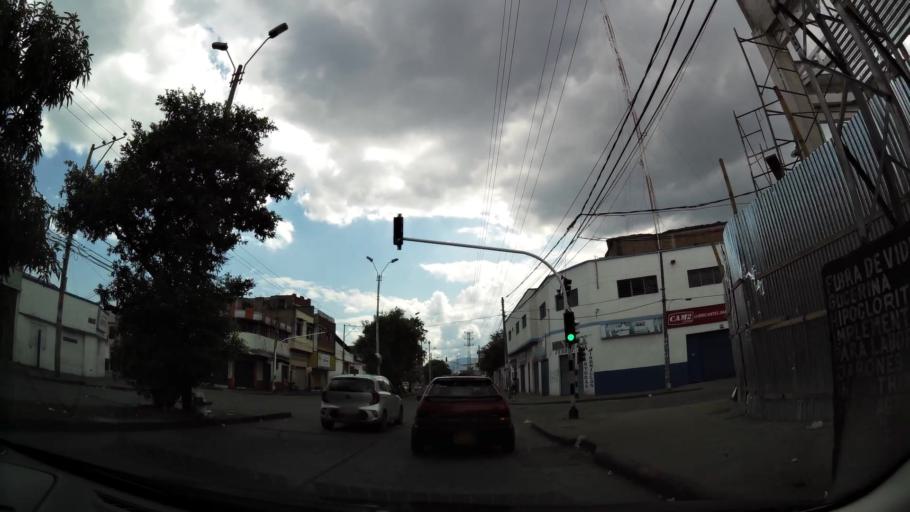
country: CO
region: Valle del Cauca
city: Cali
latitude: 3.4392
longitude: -76.5139
